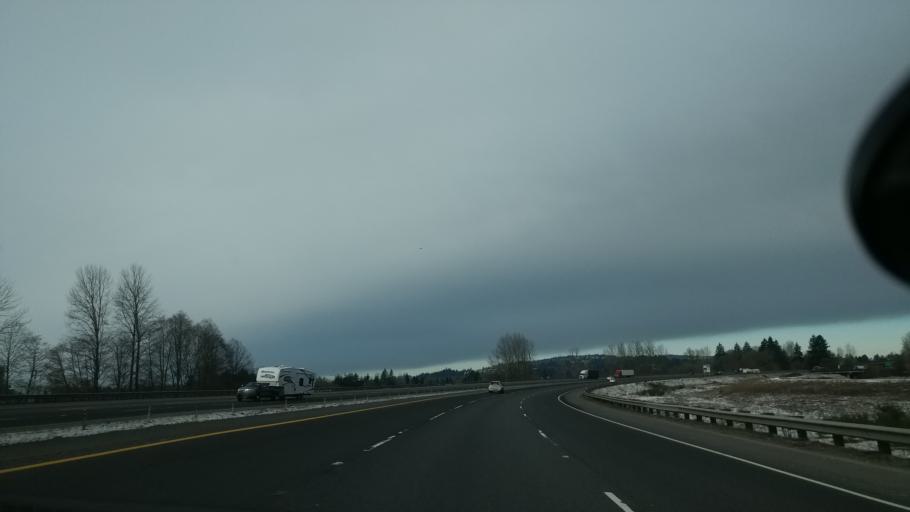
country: US
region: Washington
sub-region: Cowlitz County
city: Kelso
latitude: 46.1267
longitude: -122.8965
